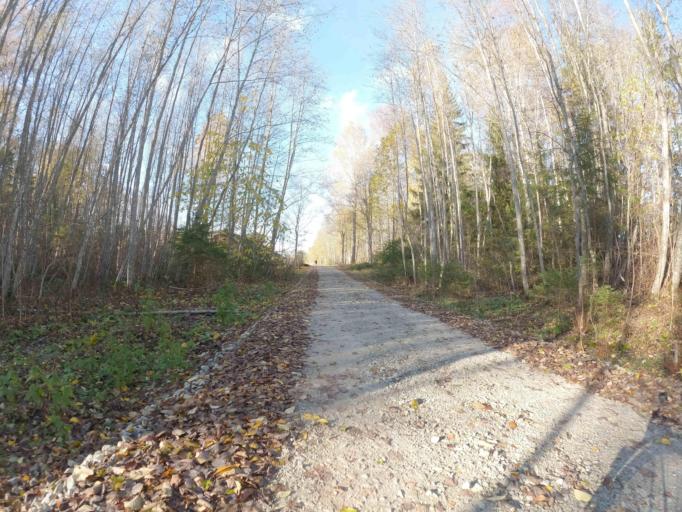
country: EE
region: Raplamaa
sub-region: Rapla vald
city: Rapla
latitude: 59.0093
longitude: 24.8083
